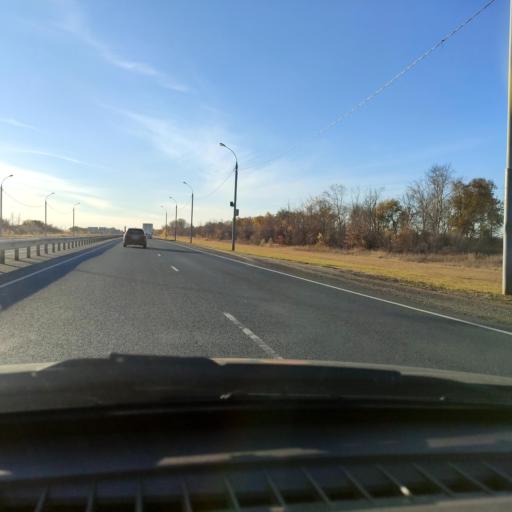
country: RU
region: Samara
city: Varlamovo
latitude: 53.1960
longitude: 48.2863
